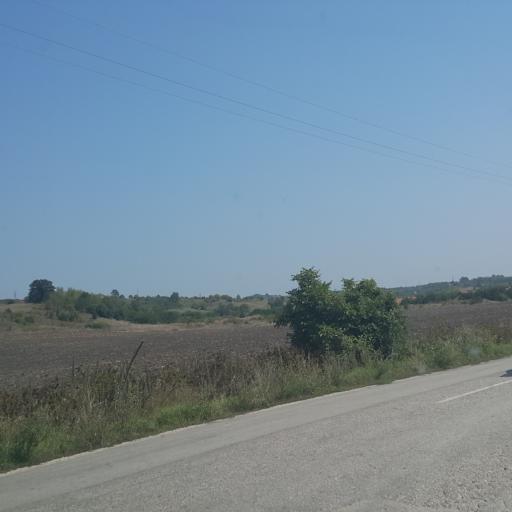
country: RS
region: Central Serbia
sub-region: Zajecarski Okrug
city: Zajecar
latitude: 43.9067
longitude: 22.2385
